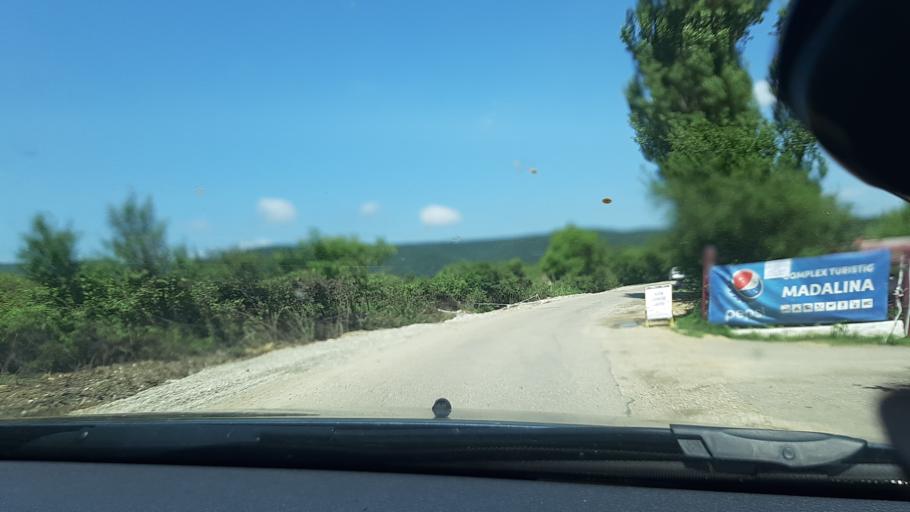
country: RO
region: Hunedoara
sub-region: Comuna Teliucu Inferior
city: Teliucu Inferior
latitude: 45.6857
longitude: 22.8707
